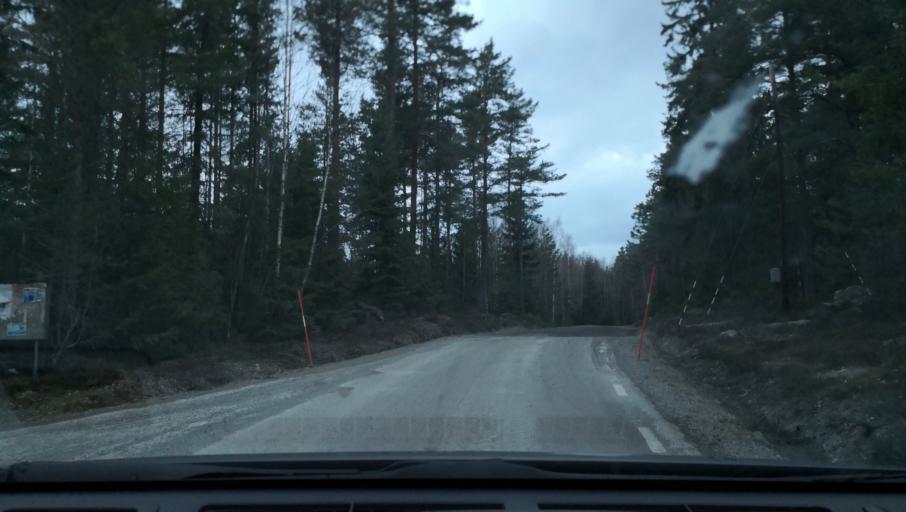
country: SE
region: Vaestmanland
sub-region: Kopings Kommun
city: Kolsva
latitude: 59.5750
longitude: 15.7135
